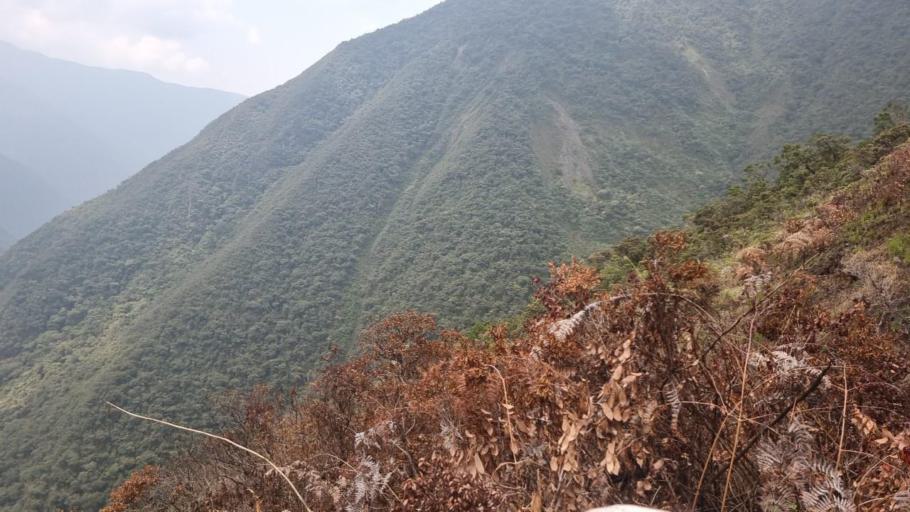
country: PE
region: Puno
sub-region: San Antonio De Putina
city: Sina
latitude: -14.7524
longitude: -68.9528
